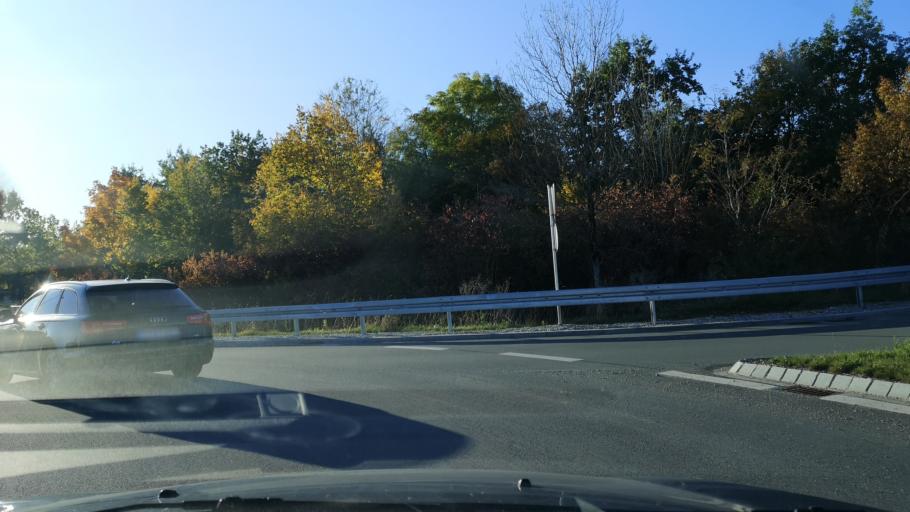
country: DE
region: Bavaria
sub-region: Upper Bavaria
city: Poing
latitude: 48.1483
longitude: 11.7869
